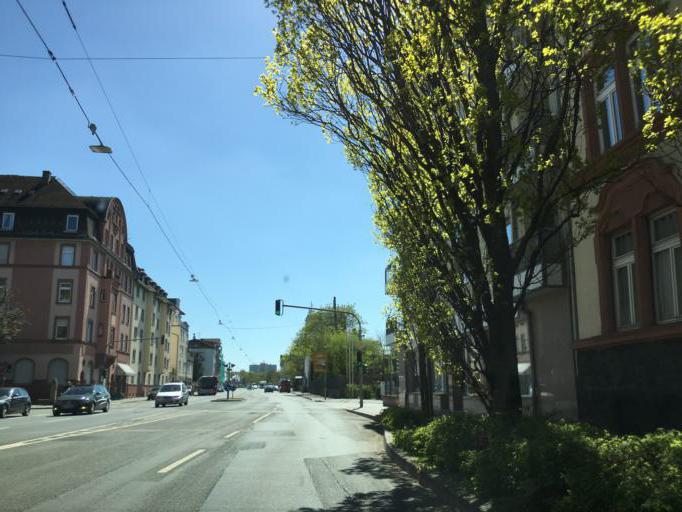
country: DE
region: Hesse
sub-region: Regierungsbezirk Darmstadt
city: Offenbach
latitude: 50.0922
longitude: 8.7690
